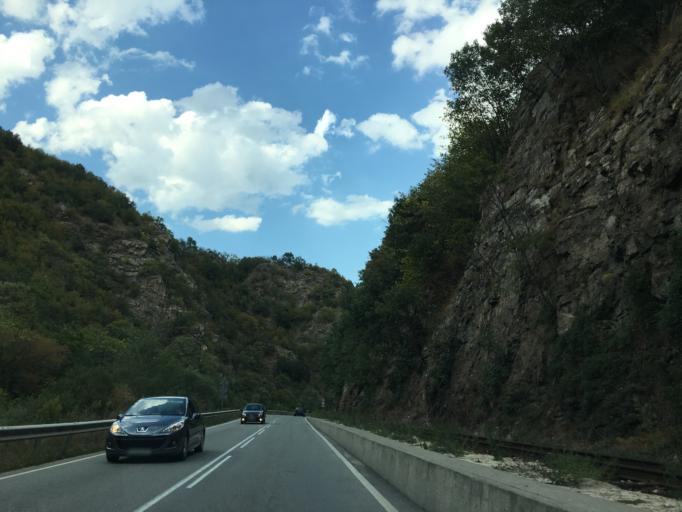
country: BG
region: Pazardzhik
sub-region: Obshtina Septemvri
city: Septemvri
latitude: 42.1267
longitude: 24.1226
